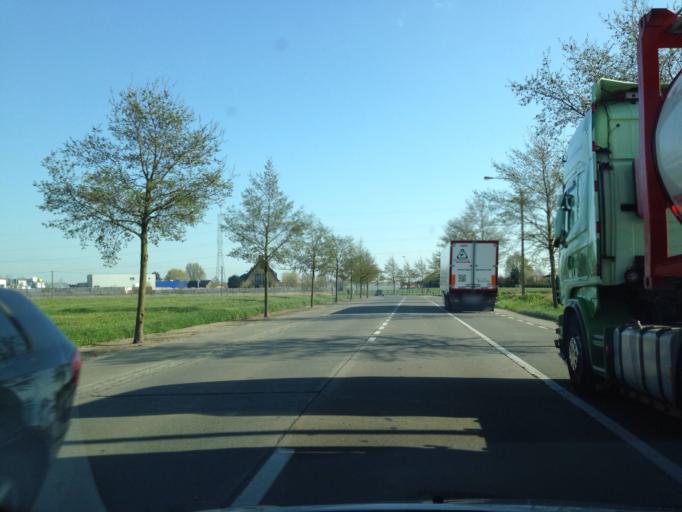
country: BE
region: Flanders
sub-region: Provincie West-Vlaanderen
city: Zedelgem
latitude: 51.1342
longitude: 3.1477
